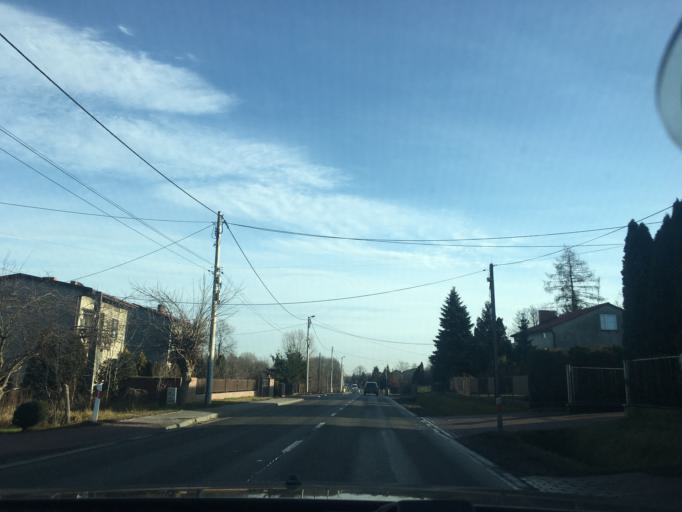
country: PL
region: Swietokrzyskie
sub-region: Powiat jedrzejowski
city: Jedrzejow
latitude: 50.6320
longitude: 20.3249
